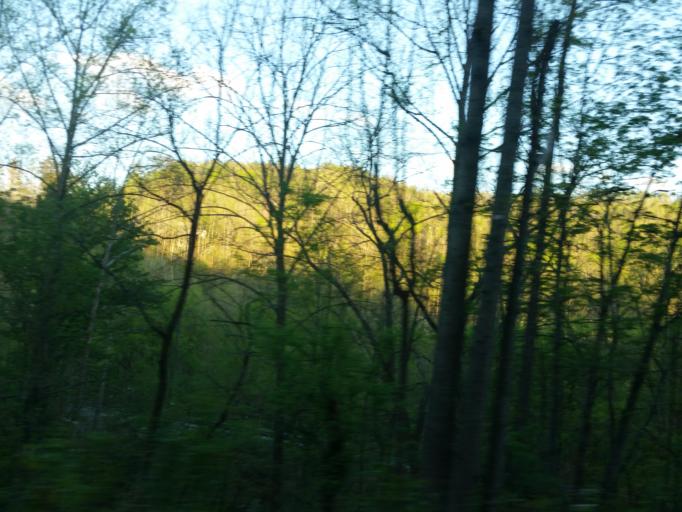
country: US
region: Tennessee
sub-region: Campbell County
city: Jellico
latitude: 36.5484
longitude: -83.9886
